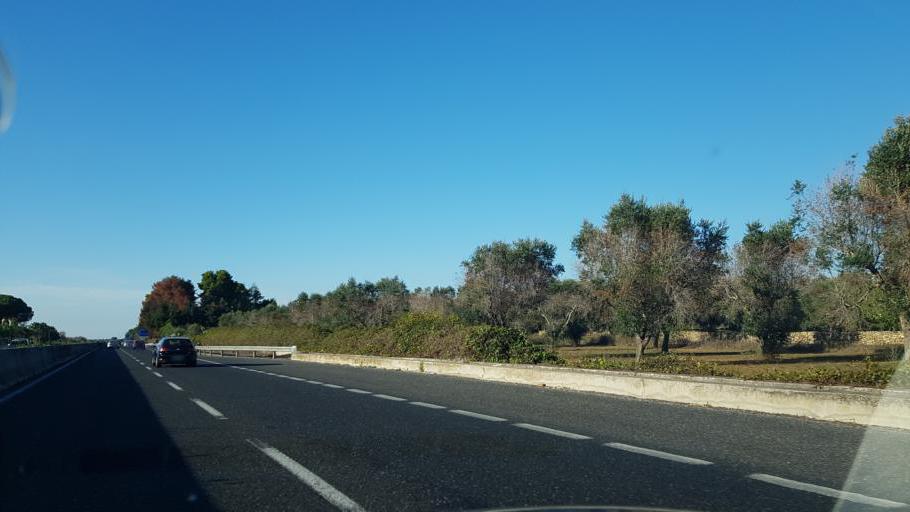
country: IT
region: Apulia
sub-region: Provincia di Brindisi
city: Torchiarolo
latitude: 40.4755
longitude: 18.0479
